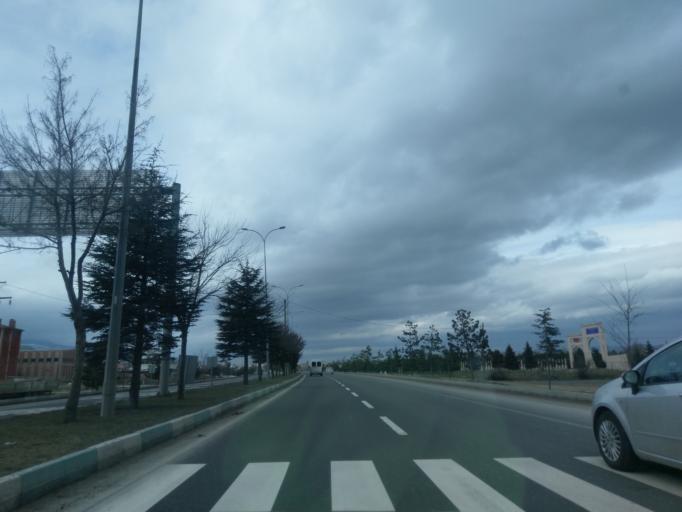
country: TR
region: Kuetahya
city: Kutahya
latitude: 39.4093
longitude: 30.0230
